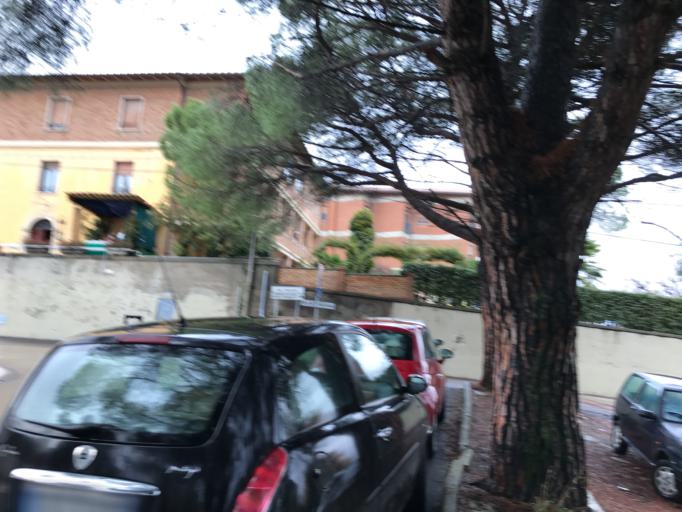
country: IT
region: Umbria
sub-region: Provincia di Perugia
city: Perugia
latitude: 43.1141
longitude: 12.4045
